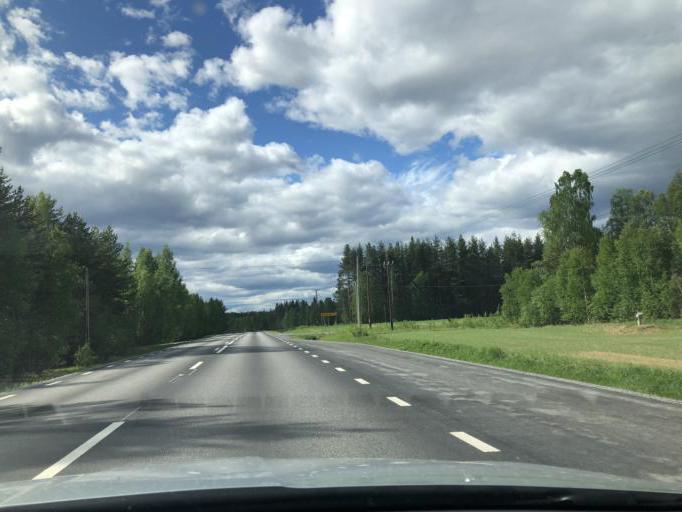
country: SE
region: Norrbotten
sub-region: Alvsbyns Kommun
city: AElvsbyn
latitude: 65.6904
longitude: 20.6879
